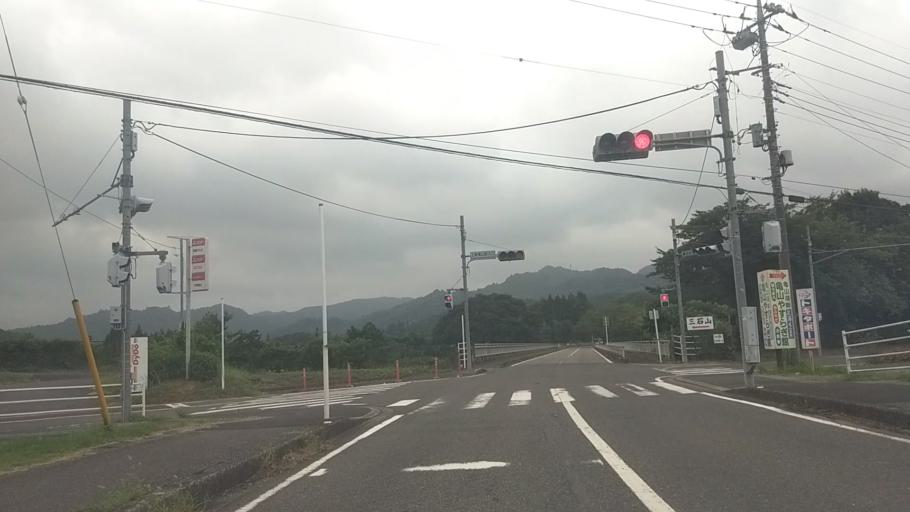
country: JP
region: Chiba
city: Kawaguchi
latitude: 35.2310
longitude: 140.0881
